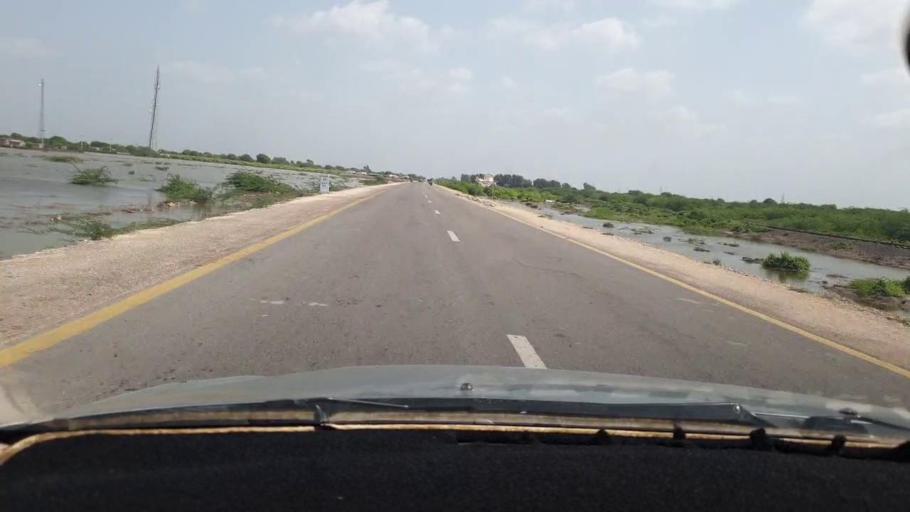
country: PK
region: Sindh
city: Digri
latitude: 25.1167
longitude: 69.1547
